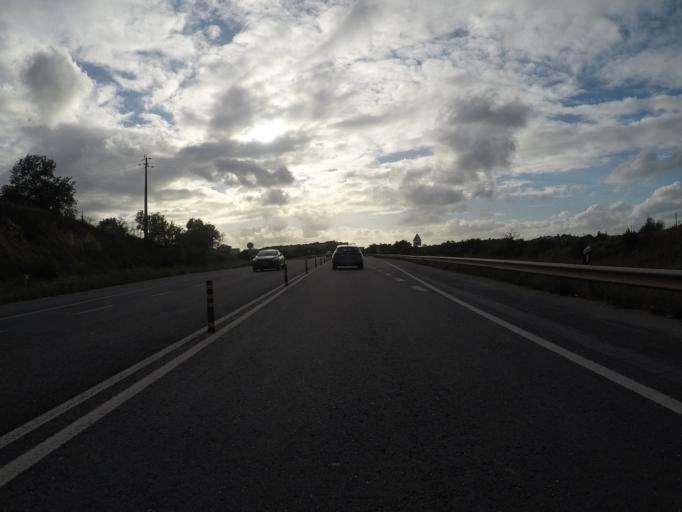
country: PT
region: Faro
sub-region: Portimao
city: Portimao
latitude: 37.1556
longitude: -8.5345
